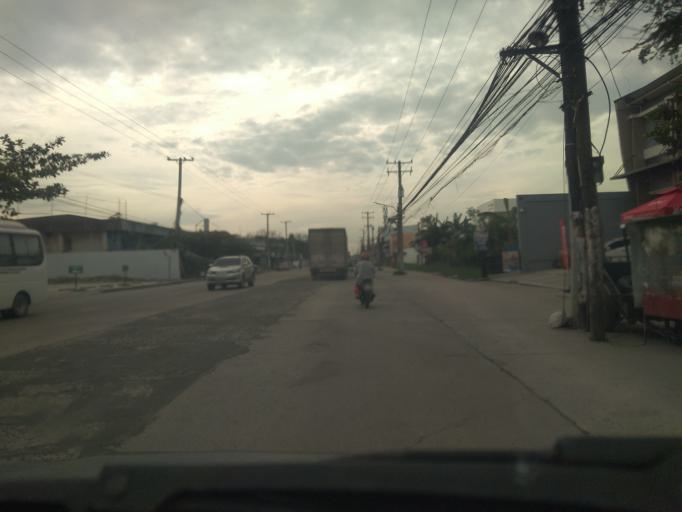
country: PH
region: Central Luzon
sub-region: Province of Pampanga
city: San Fernando
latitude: 15.0195
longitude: 120.7004
